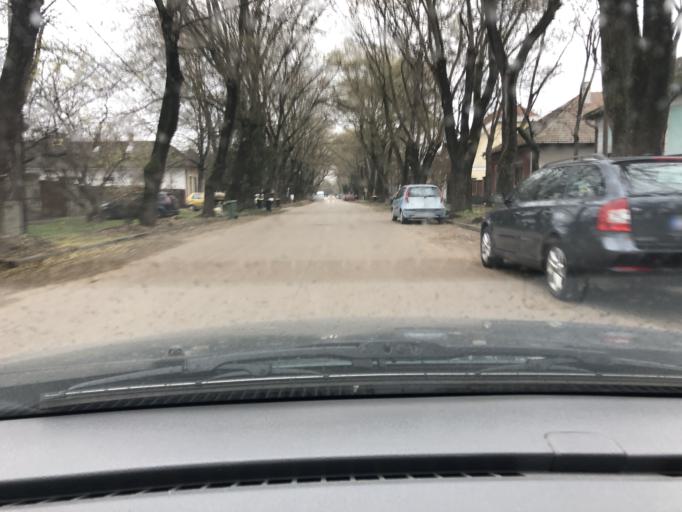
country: HU
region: Csongrad
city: Csongrad
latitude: 46.7074
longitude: 20.1451
